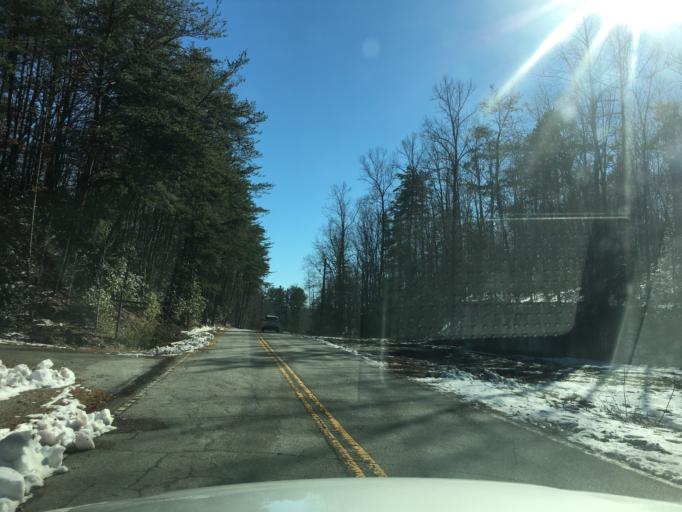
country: US
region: South Carolina
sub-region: Greenville County
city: Slater-Marietta
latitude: 35.0623
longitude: -82.6171
